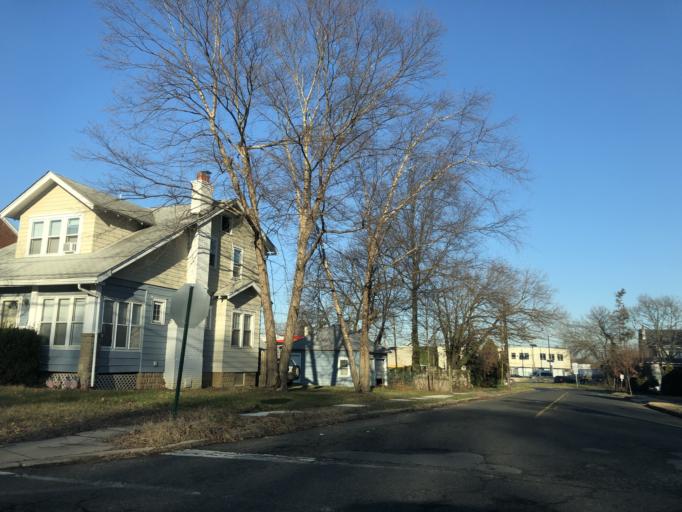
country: US
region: New Jersey
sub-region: Camden County
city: Wood-Lynne
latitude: 39.9079
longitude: -75.0934
